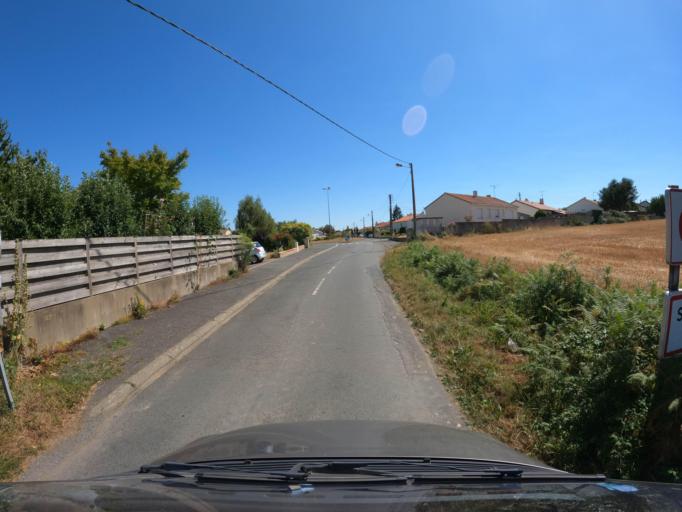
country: FR
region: Pays de la Loire
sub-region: Departement de Maine-et-Loire
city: Saint-Christophe-du-Bois
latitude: 47.0341
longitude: -0.9479
